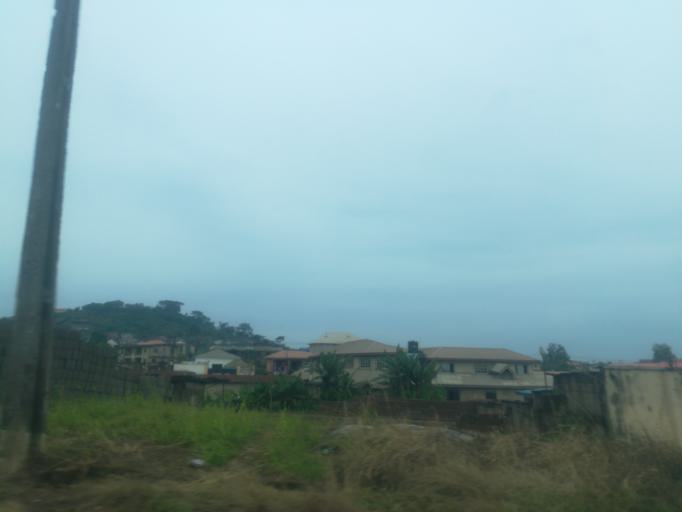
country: NG
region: Oyo
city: Egbeda
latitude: 7.3837
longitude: 3.9902
